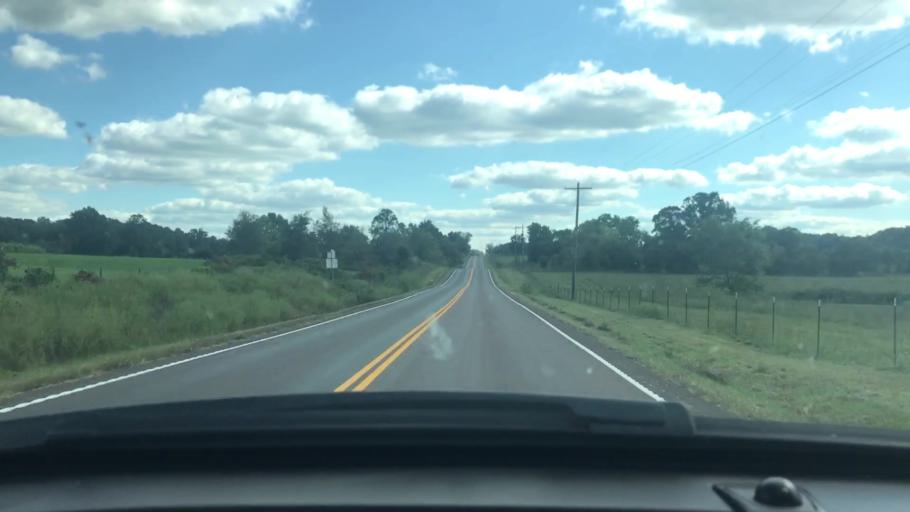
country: US
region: Missouri
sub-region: Wright County
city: Mountain Grove
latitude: 37.2412
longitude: -92.3005
